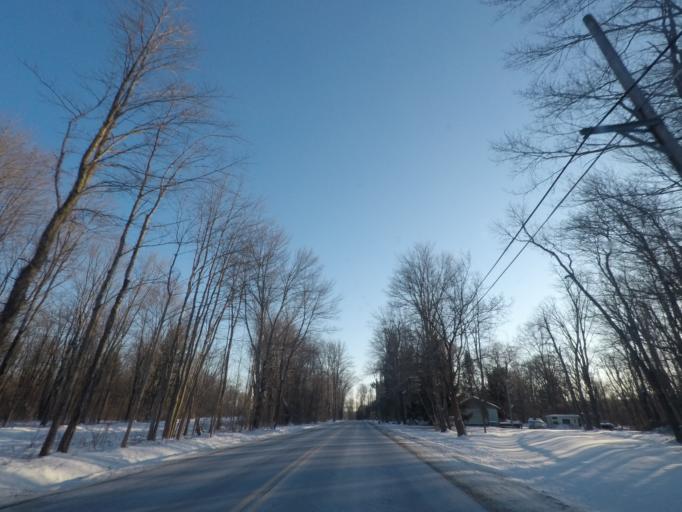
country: US
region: New York
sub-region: Saratoga County
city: Mechanicville
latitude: 42.8599
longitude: -73.6717
